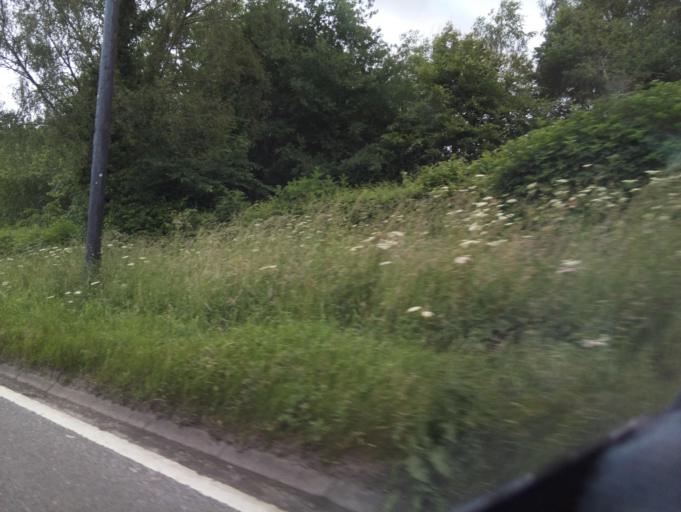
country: GB
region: England
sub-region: Staffordshire
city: Mayfield
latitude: 53.0041
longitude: -1.7499
